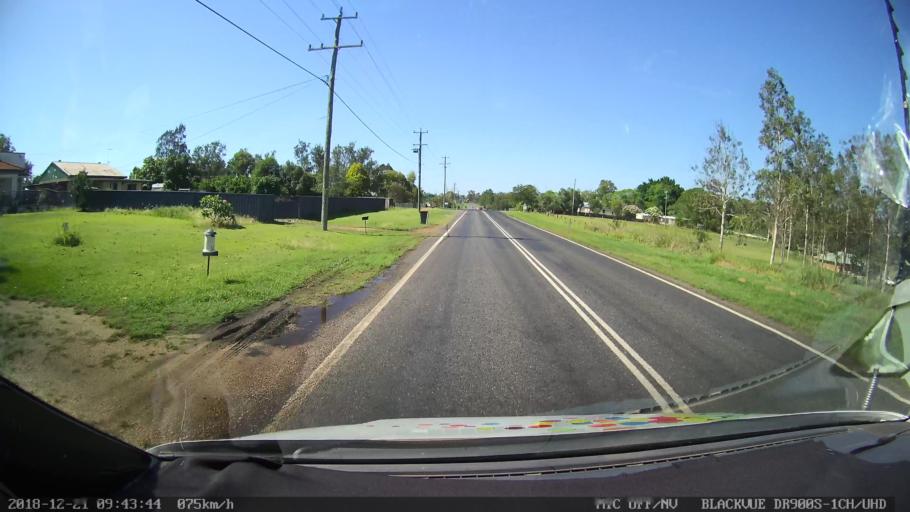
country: AU
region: New South Wales
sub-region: Clarence Valley
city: Grafton
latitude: -29.6101
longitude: 152.9353
